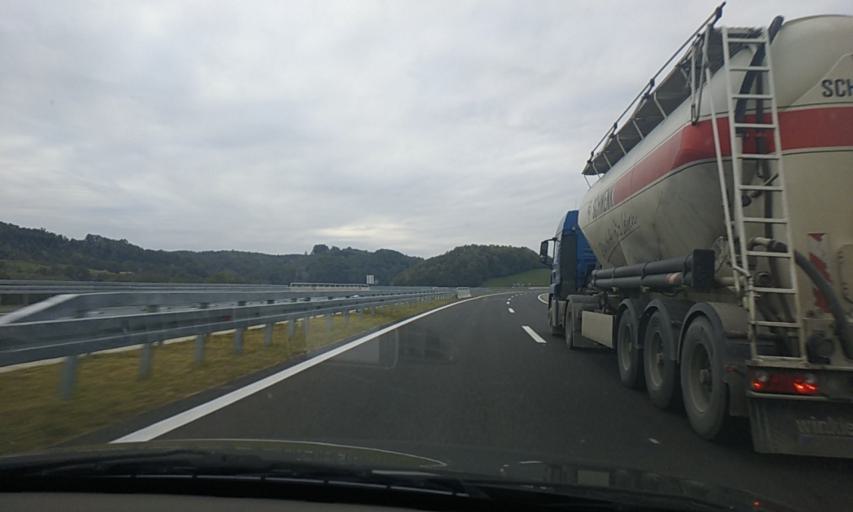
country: BA
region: Republika Srpska
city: Maglajani
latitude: 44.8549
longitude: 17.4570
